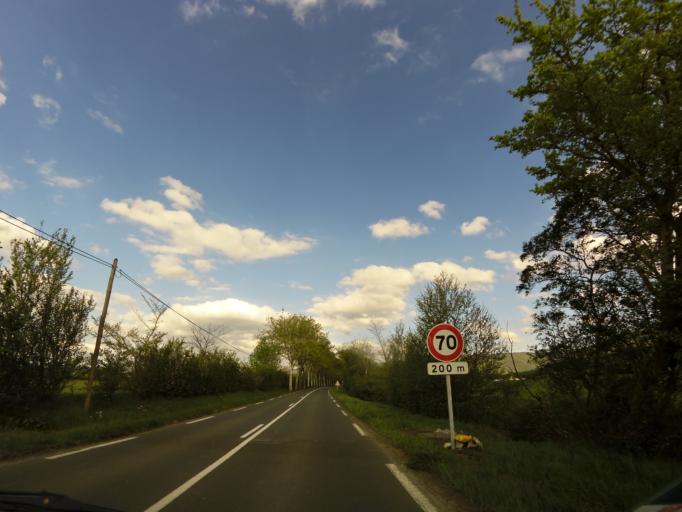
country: FR
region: Midi-Pyrenees
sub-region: Departement de la Haute-Garonne
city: Revel
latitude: 43.4532
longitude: 2.0320
